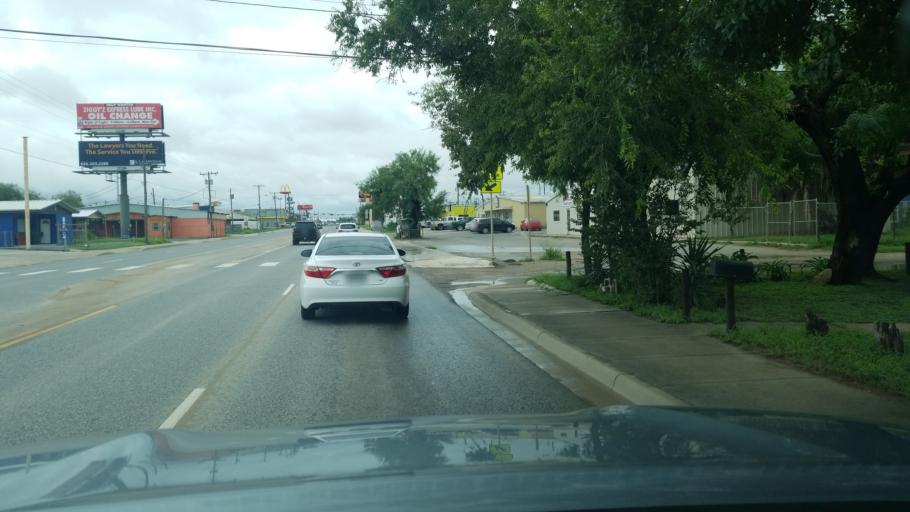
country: US
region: Texas
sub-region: Dimmit County
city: Carrizo Springs
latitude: 28.5260
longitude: -99.8553
